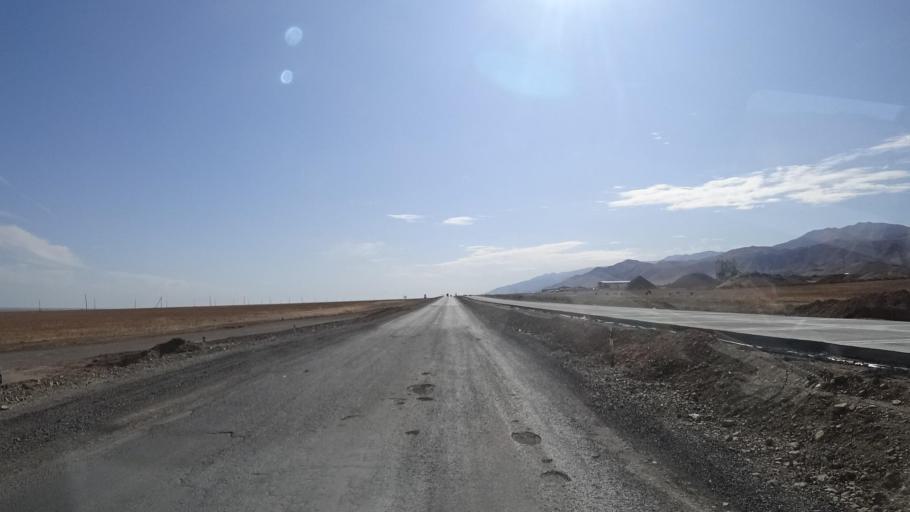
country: KG
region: Chuy
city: Ivanovka
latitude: 43.3921
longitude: 75.1372
